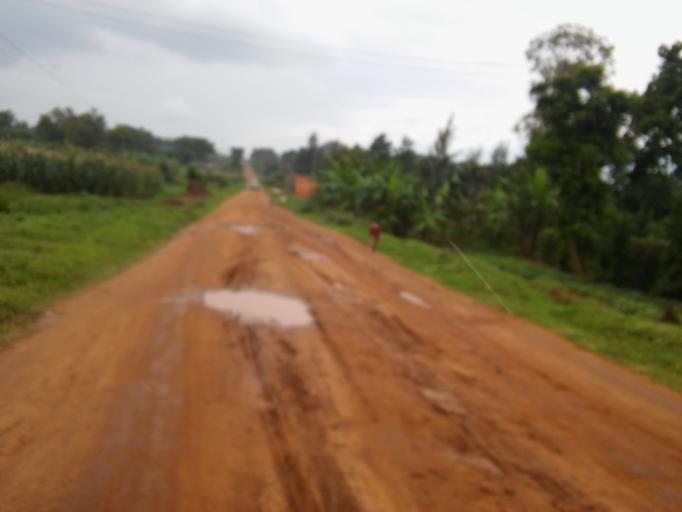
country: UG
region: Eastern Region
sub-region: Mbale District
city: Mbale
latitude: 1.0184
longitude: 34.1841
